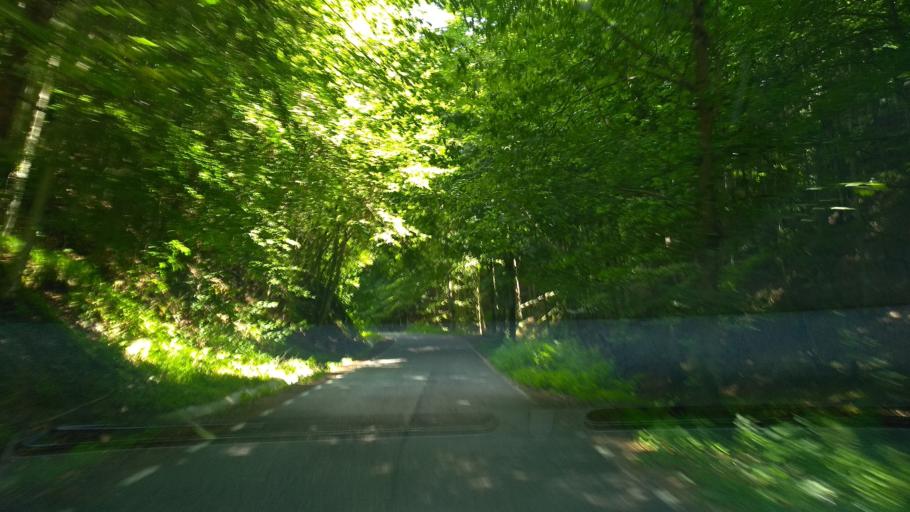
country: RO
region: Hunedoara
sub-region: Comuna Orastioara de Sus
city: Orastioara de Sus
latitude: 45.6219
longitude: 23.2716
